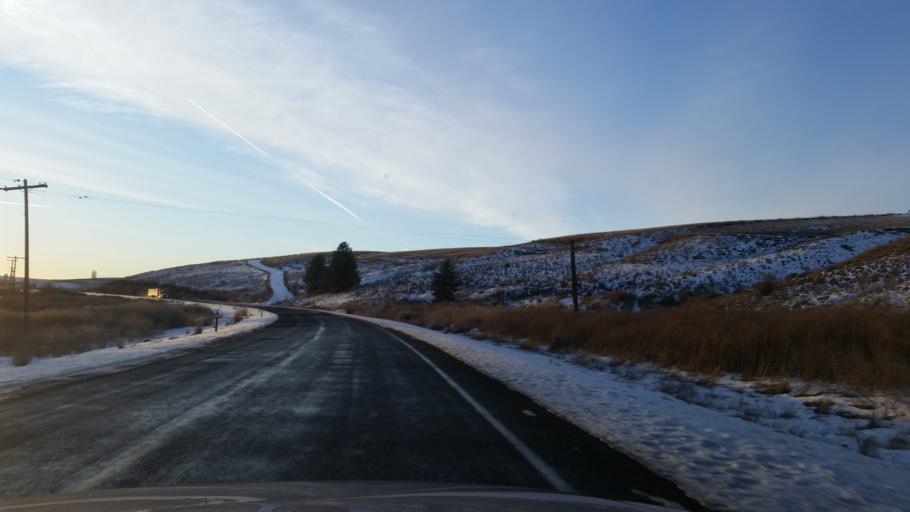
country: US
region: Washington
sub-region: Spokane County
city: Cheney
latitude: 47.1181
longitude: -117.6823
